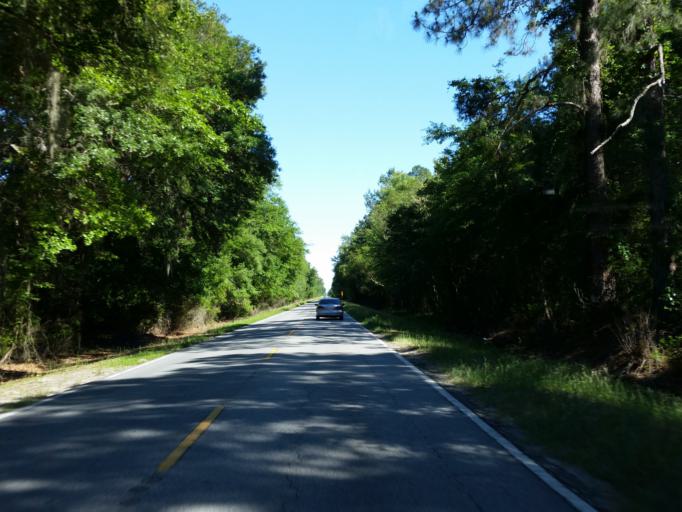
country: US
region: Georgia
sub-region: Echols County
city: Statenville
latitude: 30.6684
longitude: -83.1632
